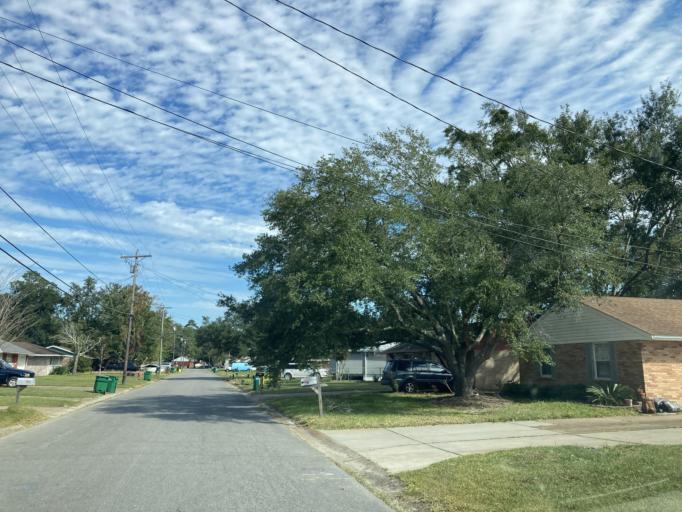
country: US
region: Mississippi
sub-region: Jackson County
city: Saint Martin
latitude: 30.4448
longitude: -88.8723
